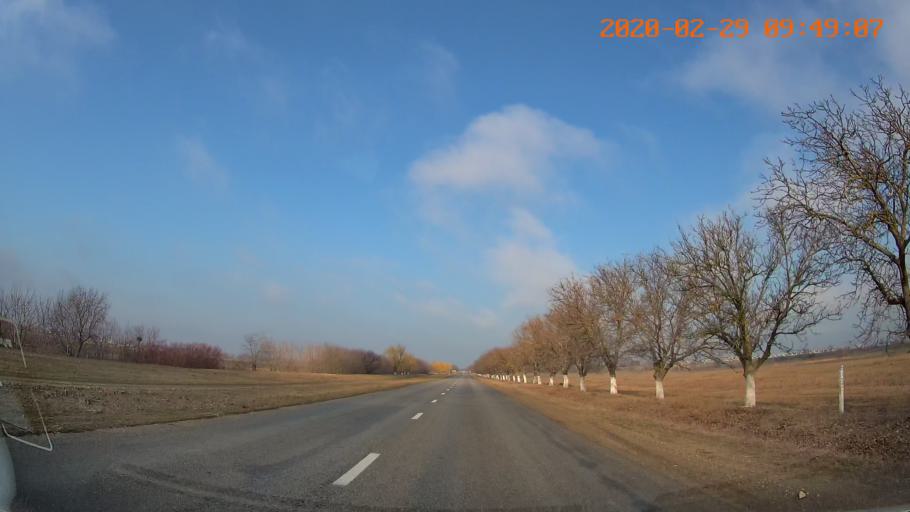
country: MD
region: Telenesti
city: Crasnoe
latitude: 46.6948
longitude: 29.7770
